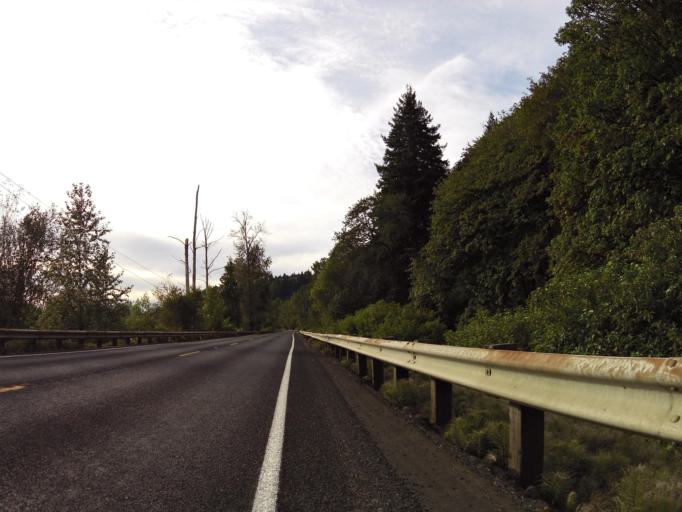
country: US
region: Washington
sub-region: Cowlitz County
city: West Longview
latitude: 46.1855
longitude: -123.0824
